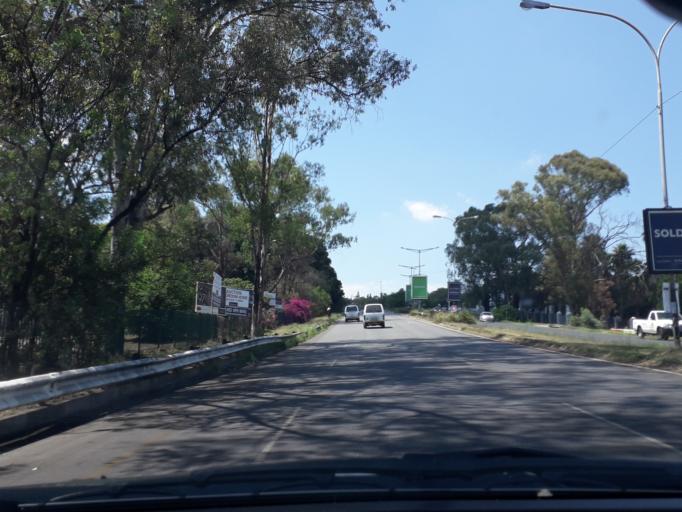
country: ZA
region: Gauteng
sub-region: City of Johannesburg Metropolitan Municipality
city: Johannesburg
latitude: -26.1216
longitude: 28.0322
